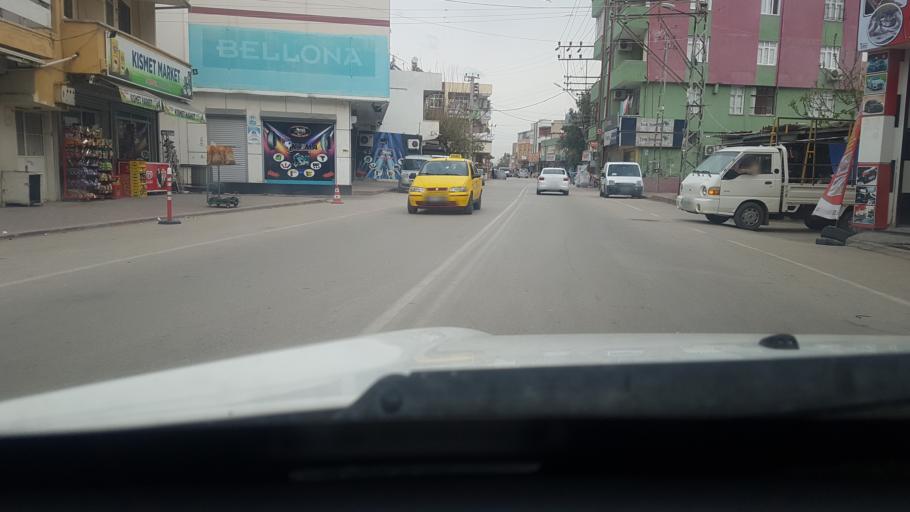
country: TR
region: Adana
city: Seyhan
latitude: 37.0150
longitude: 35.2760
